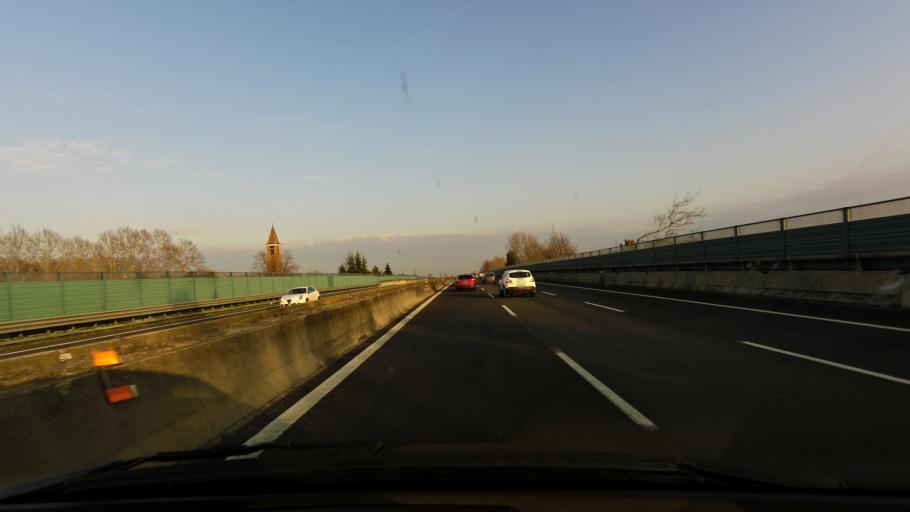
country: IT
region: Emilia-Romagna
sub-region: Forli-Cesena
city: Forli
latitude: 44.2683
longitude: 12.0451
